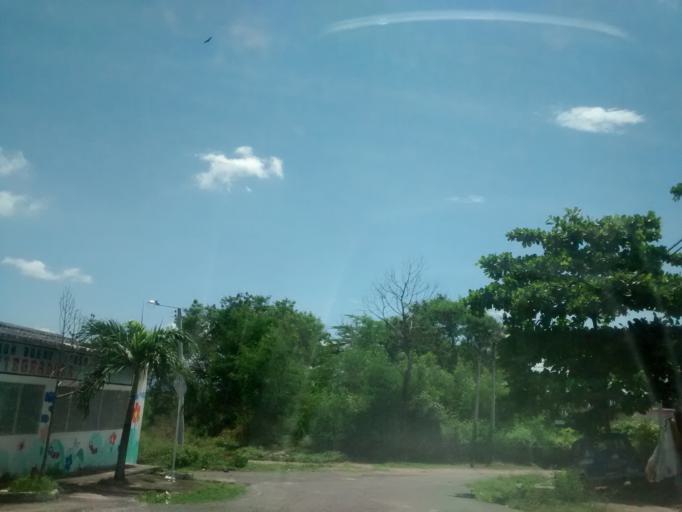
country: CO
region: Cundinamarca
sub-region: Girardot
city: Girardot City
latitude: 4.3065
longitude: -74.7958
